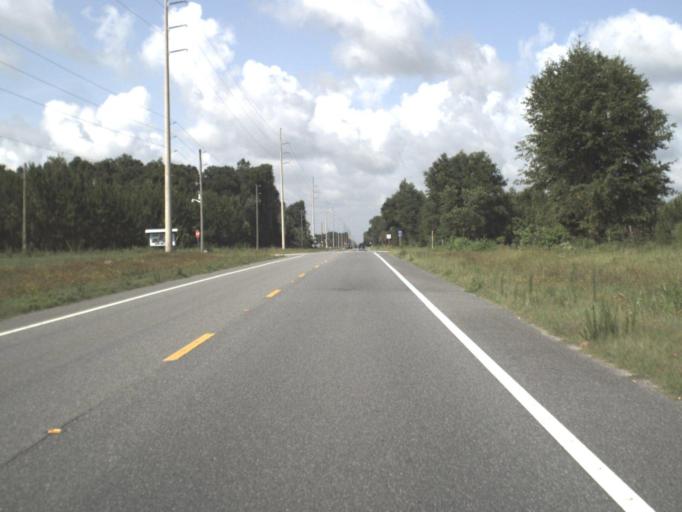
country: US
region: Florida
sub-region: Suwannee County
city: Wellborn
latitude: 30.0452
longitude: -82.8079
